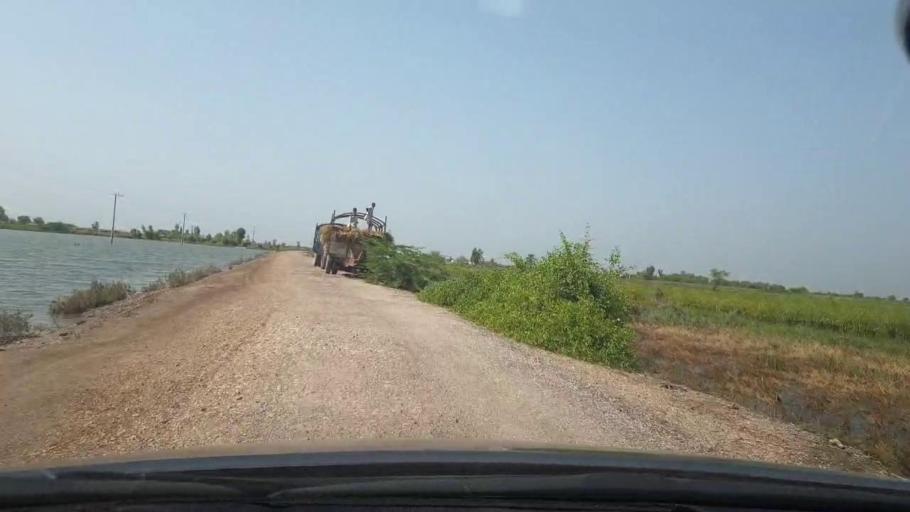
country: PK
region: Sindh
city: Tando Bago
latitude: 24.7133
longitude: 69.0891
